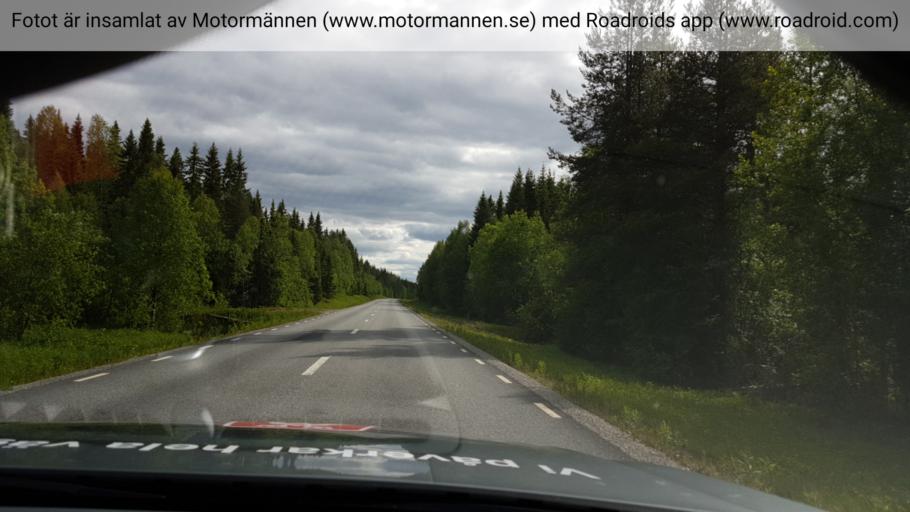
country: SE
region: Jaemtland
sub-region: Stroemsunds Kommun
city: Stroemsund
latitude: 64.0177
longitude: 15.5244
